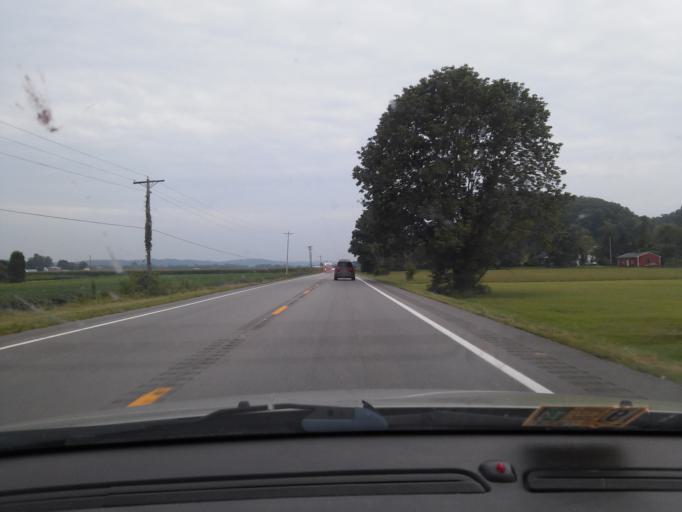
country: US
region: West Virginia
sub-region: Putnam County
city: Buffalo
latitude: 38.6731
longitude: -81.9663
